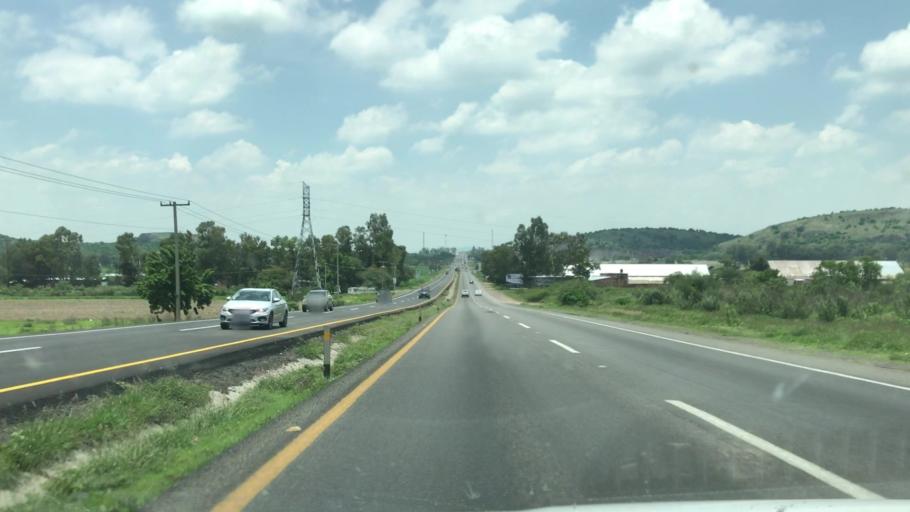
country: MX
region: Guanajuato
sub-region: Irapuato
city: San Ignacio de Rivera (Ojo de Agua)
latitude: 20.5442
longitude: -101.4552
